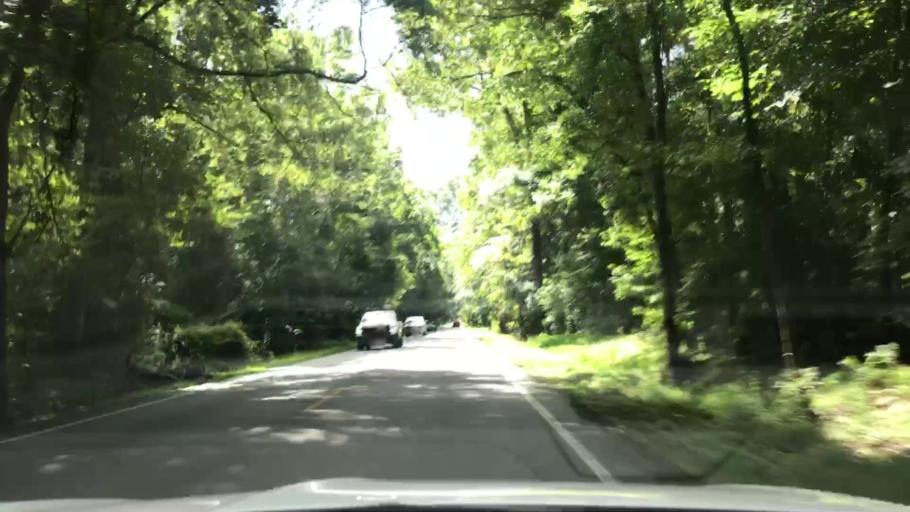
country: US
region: South Carolina
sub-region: Berkeley County
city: Hanahan
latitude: 32.8737
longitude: -80.0935
